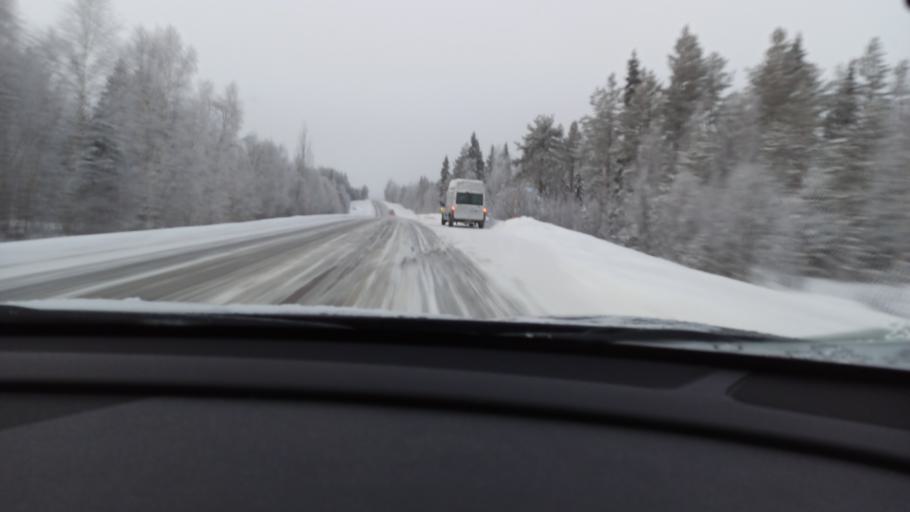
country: FI
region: Lapland
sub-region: Pohjois-Lappi
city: Sodankylae
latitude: 66.9287
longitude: 26.2361
